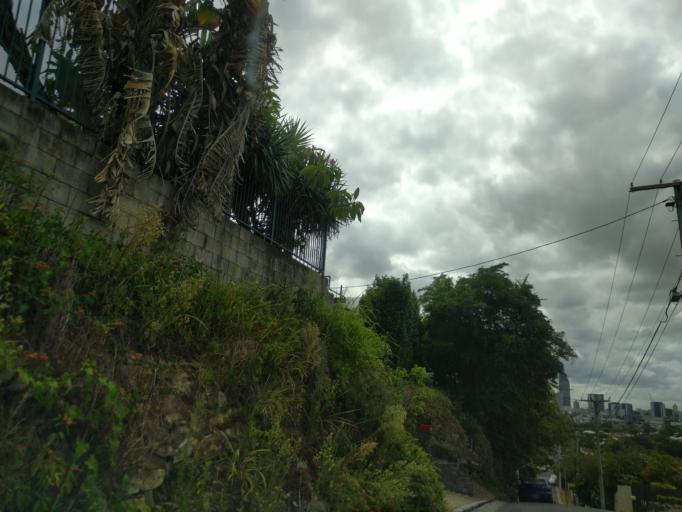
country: AU
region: Queensland
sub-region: Brisbane
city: Milton
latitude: -27.4688
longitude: 152.9914
